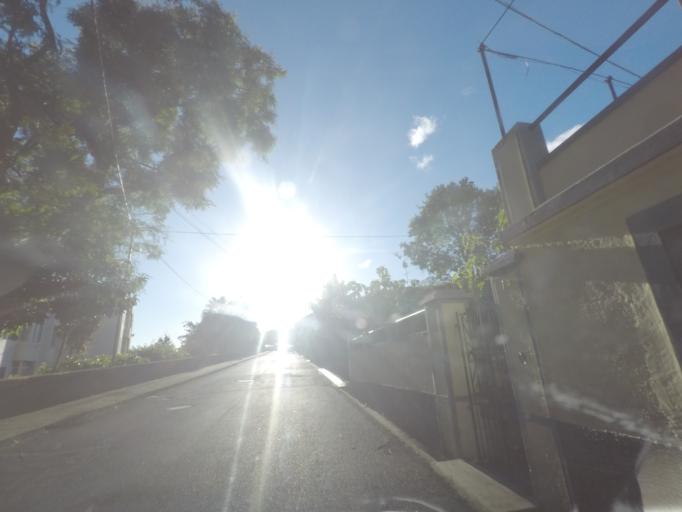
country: PT
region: Madeira
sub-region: Funchal
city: Nossa Senhora do Monte
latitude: 32.6654
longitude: -16.9284
